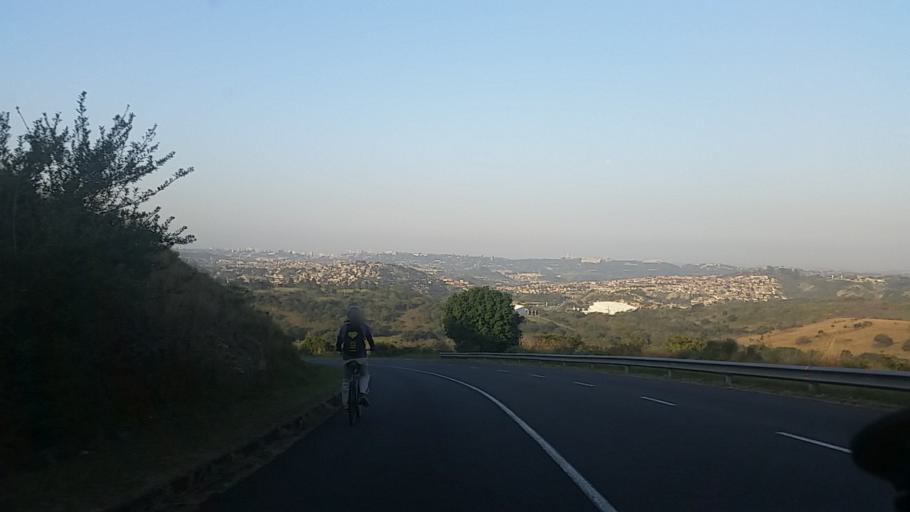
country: ZA
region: KwaZulu-Natal
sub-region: eThekwini Metropolitan Municipality
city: Berea
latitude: -29.8552
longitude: 30.9266
